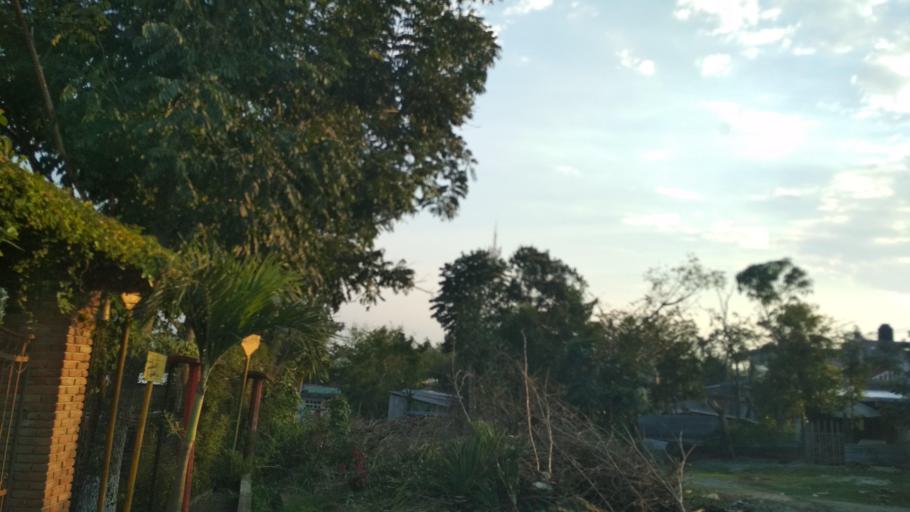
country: MM
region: Shan
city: Taunggyi
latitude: 20.4070
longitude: 97.3370
